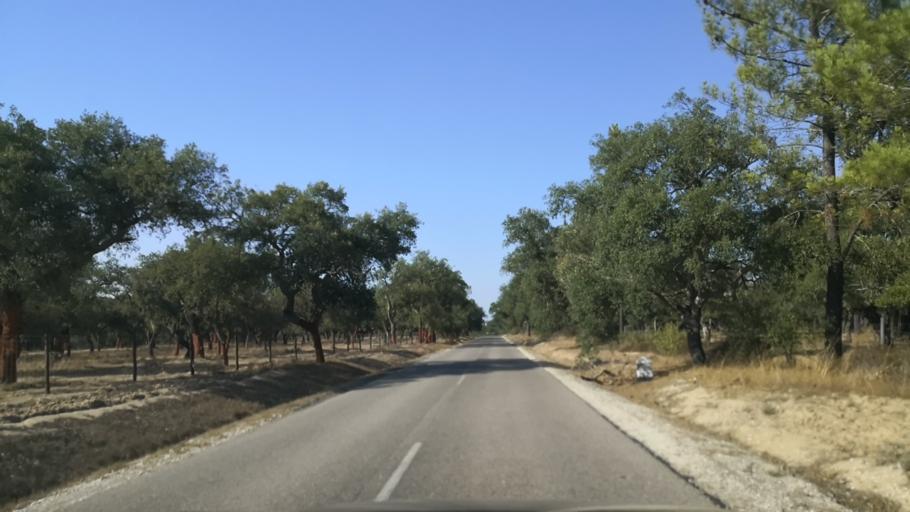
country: PT
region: Santarem
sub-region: Coruche
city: Coruche
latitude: 38.9211
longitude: -8.5238
